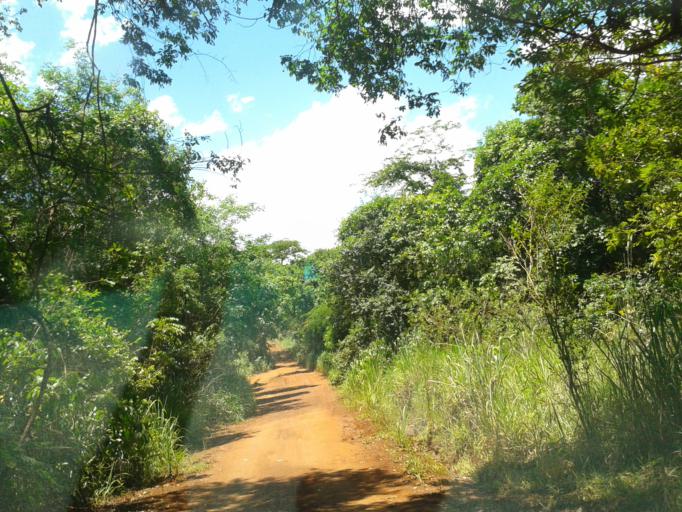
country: BR
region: Minas Gerais
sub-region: Centralina
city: Centralina
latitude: -18.6993
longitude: -49.1707
